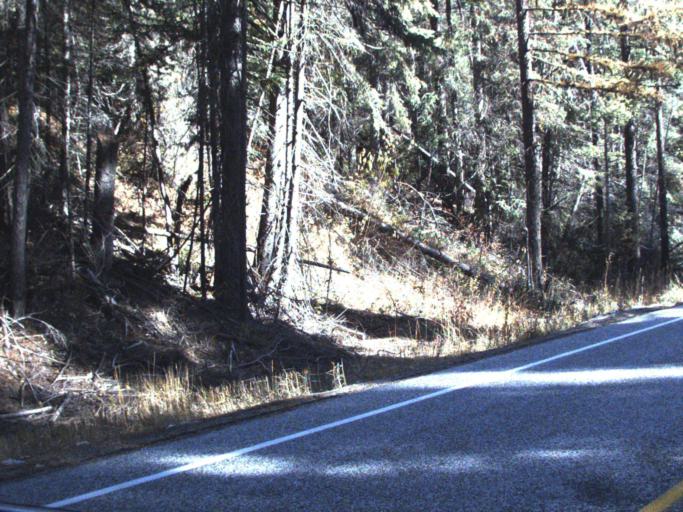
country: US
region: Washington
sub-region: Ferry County
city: Republic
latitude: 48.6216
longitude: -118.4060
